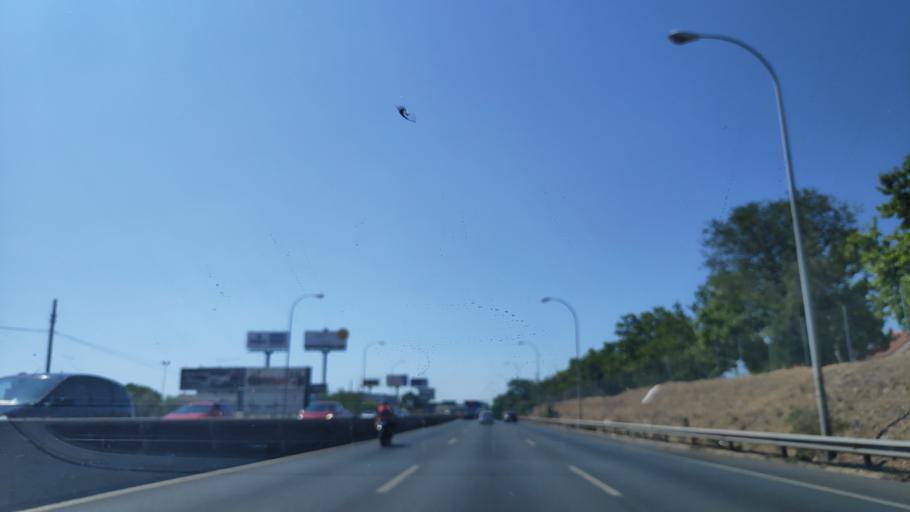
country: ES
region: Madrid
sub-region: Provincia de Madrid
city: Getafe
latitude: 40.2903
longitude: -3.7413
